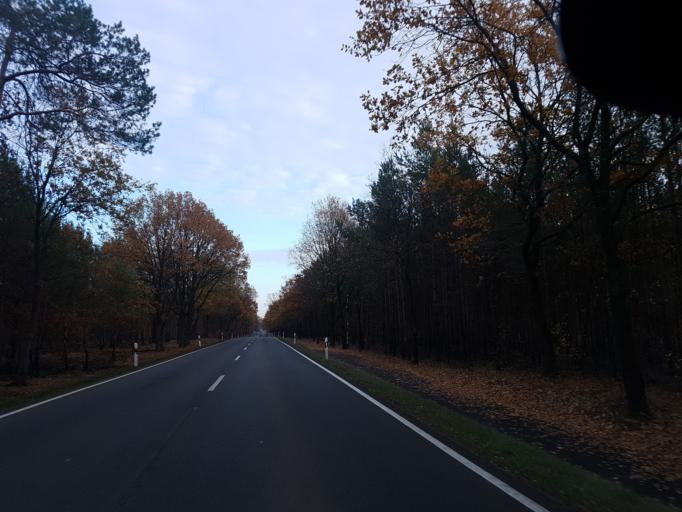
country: DE
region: Brandenburg
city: Treuenbrietzen
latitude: 52.0401
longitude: 12.9284
